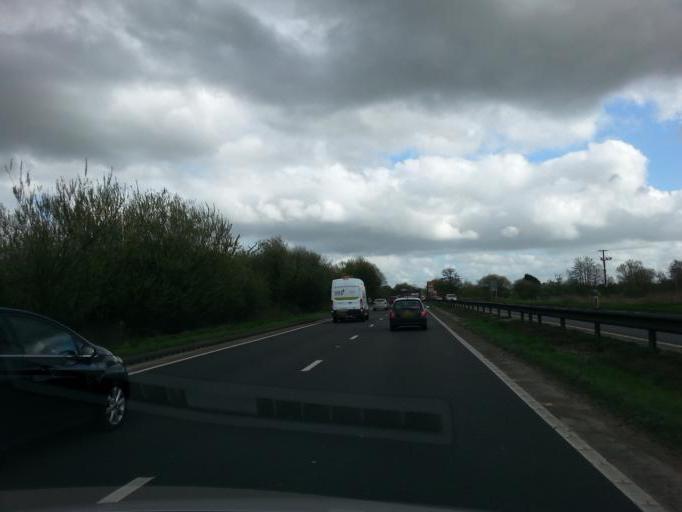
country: GB
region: England
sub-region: Hampshire
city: Andover
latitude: 51.1847
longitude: -1.4024
